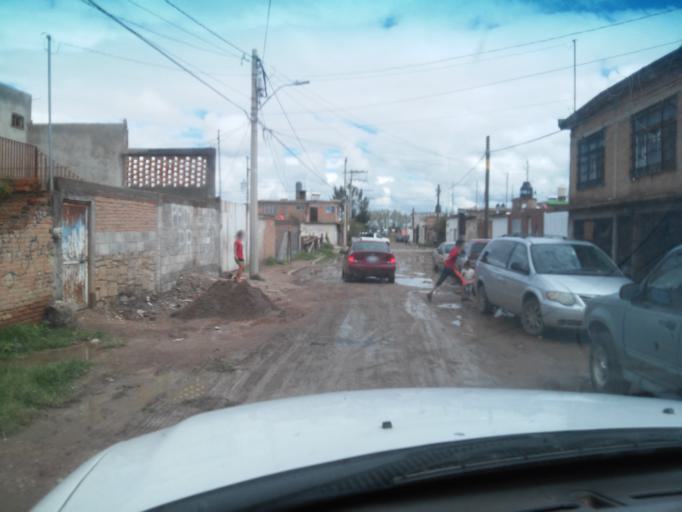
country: MX
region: Durango
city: Victoria de Durango
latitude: 24.0173
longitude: -104.6123
